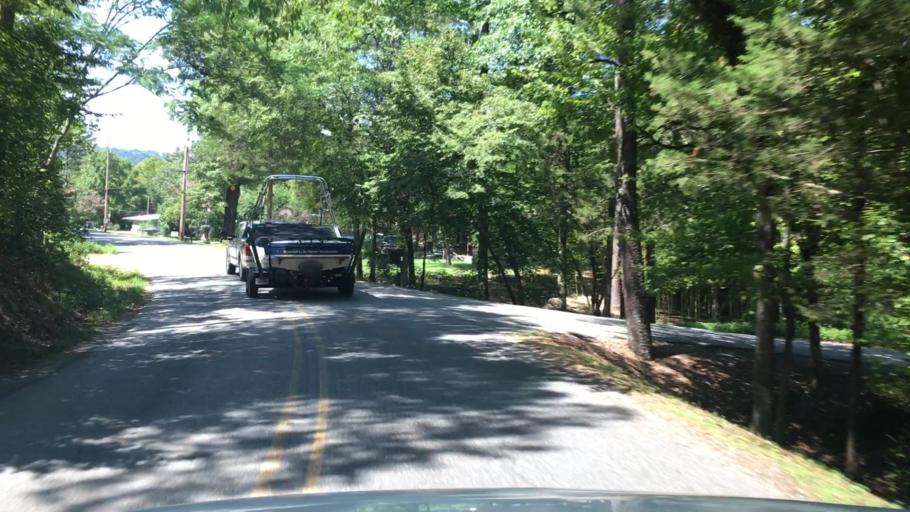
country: US
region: Arkansas
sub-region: Garland County
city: Piney
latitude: 34.5278
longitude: -93.3356
